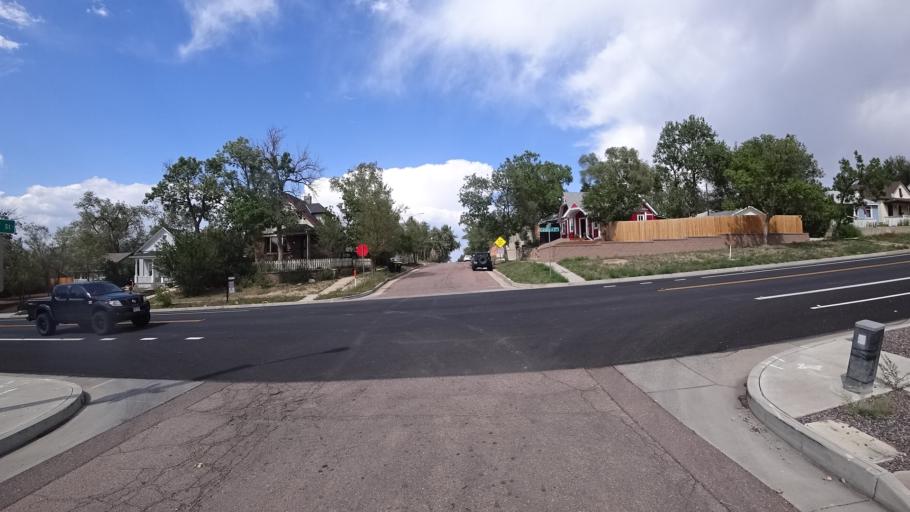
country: US
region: Colorado
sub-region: El Paso County
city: Colorado Springs
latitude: 38.8276
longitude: -104.8107
